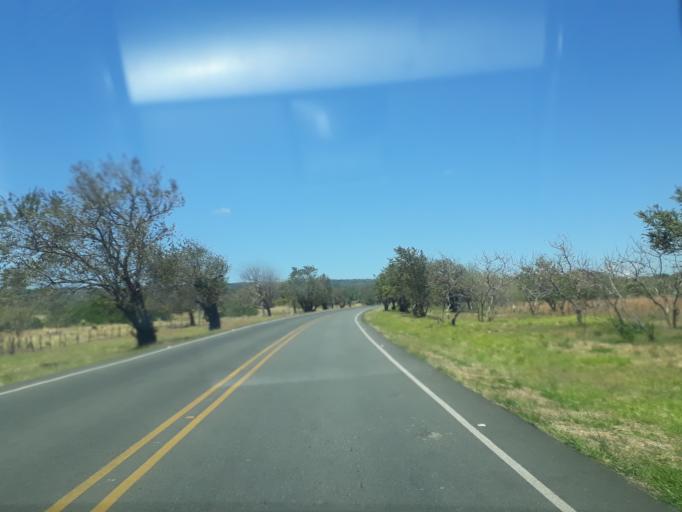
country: CR
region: Guanacaste
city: Liberia
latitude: 10.8290
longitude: -85.5549
